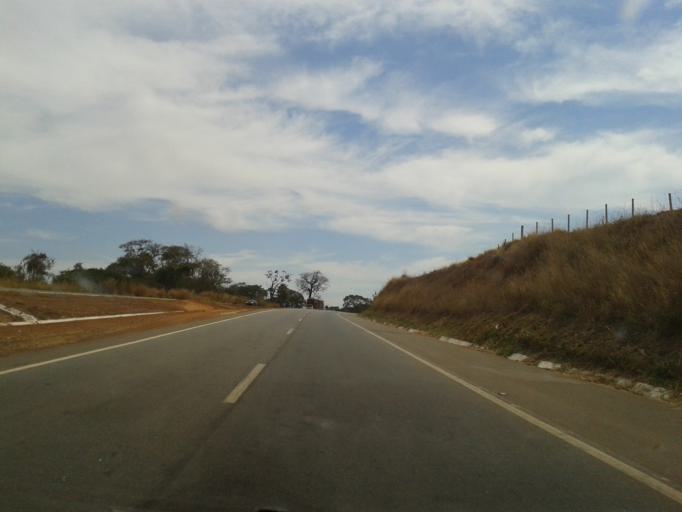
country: BR
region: Goias
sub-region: Itaberai
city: Itaberai
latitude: -16.1474
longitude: -49.6340
